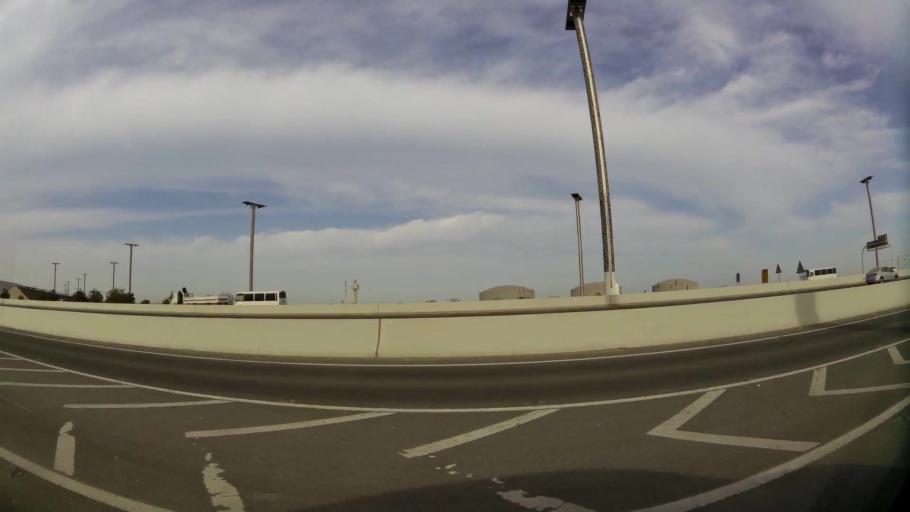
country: QA
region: Al Wakrah
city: Al Wakrah
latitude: 25.2359
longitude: 51.5924
